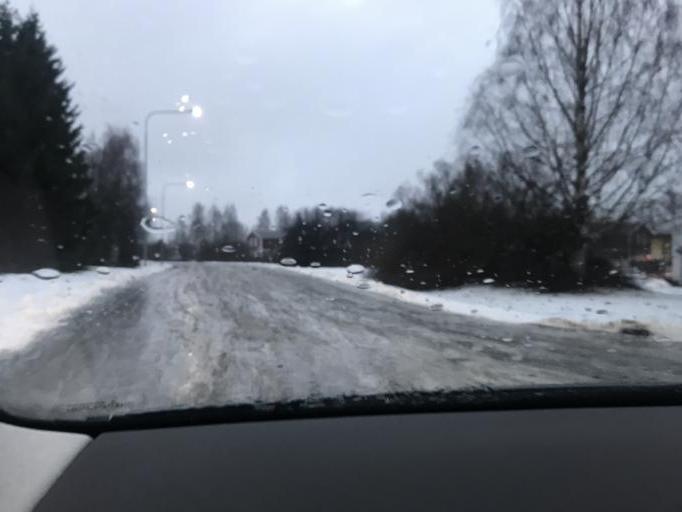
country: SE
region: Norrbotten
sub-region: Lulea Kommun
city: Sodra Sunderbyn
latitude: 65.6496
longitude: 21.9634
